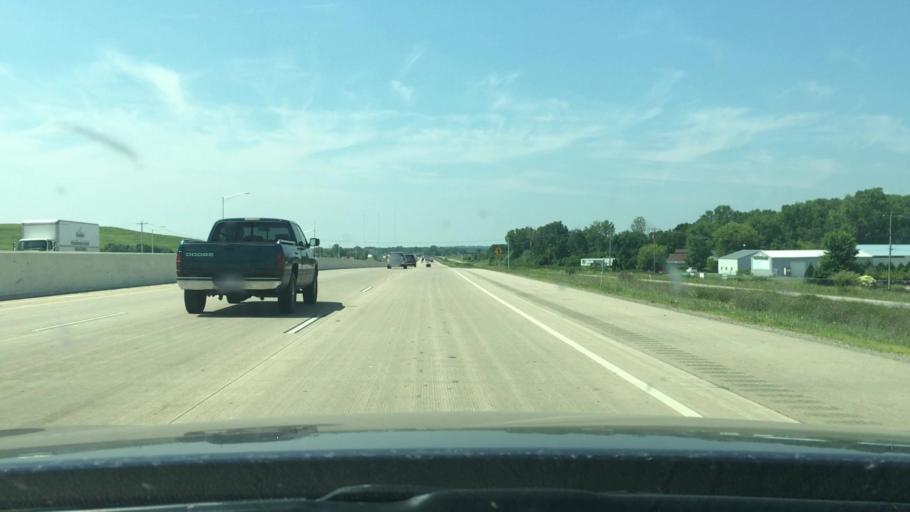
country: US
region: Wisconsin
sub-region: Winnebago County
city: Oshkosh
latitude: 44.0964
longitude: -88.5443
